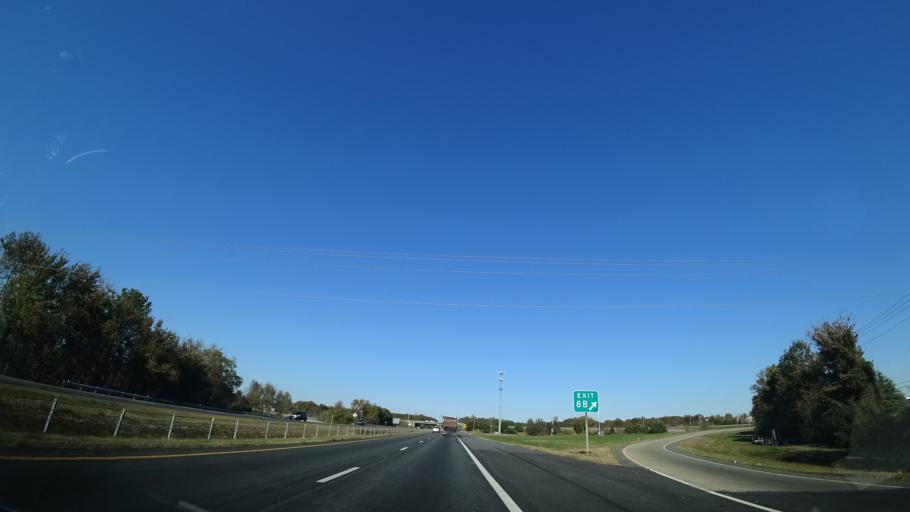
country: US
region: Virginia
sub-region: City of Portsmouth
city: Portsmouth Heights
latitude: 36.8830
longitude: -76.4307
